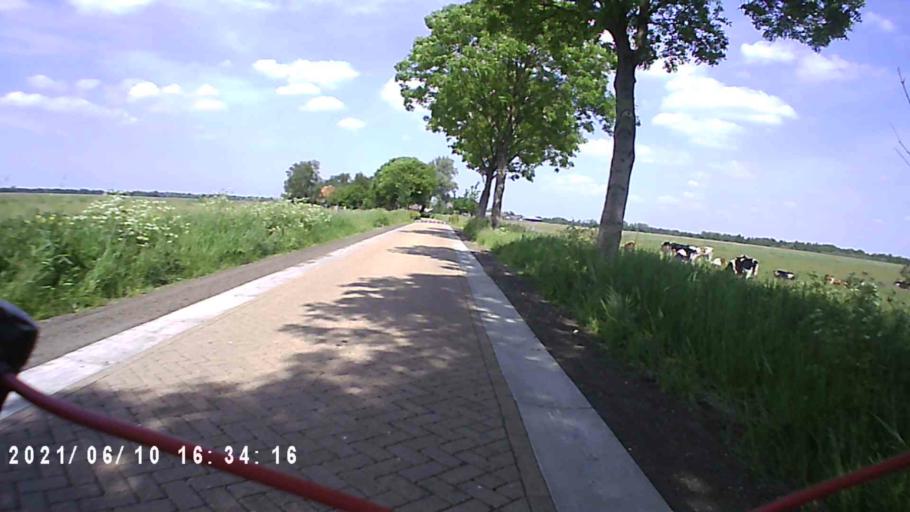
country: NL
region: Friesland
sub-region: Gemeente Achtkarspelen
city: Buitenpost
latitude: 53.2311
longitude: 6.1308
